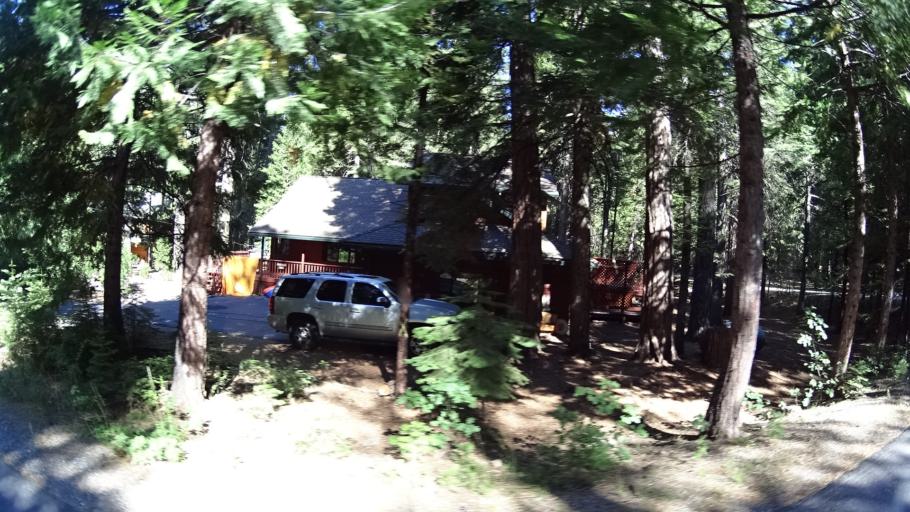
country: US
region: California
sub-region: Calaveras County
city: Arnold
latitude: 38.2916
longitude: -120.2688
